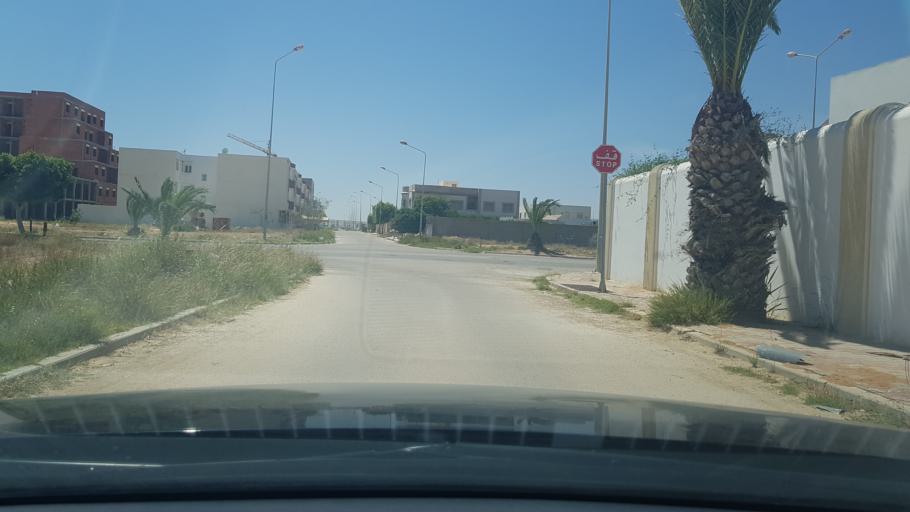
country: TN
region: Safaqis
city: Al Qarmadah
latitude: 34.8358
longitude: 10.7617
